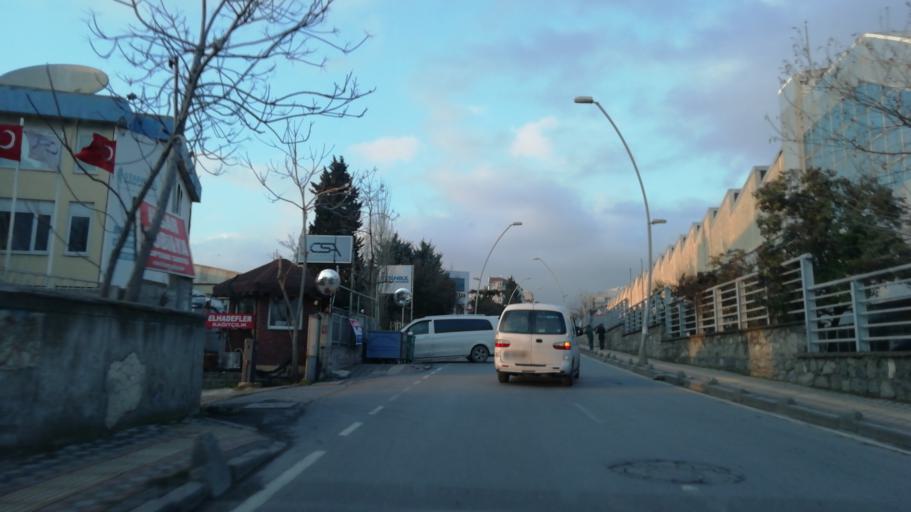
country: TR
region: Istanbul
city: Bahcelievler
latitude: 41.0049
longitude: 28.8215
